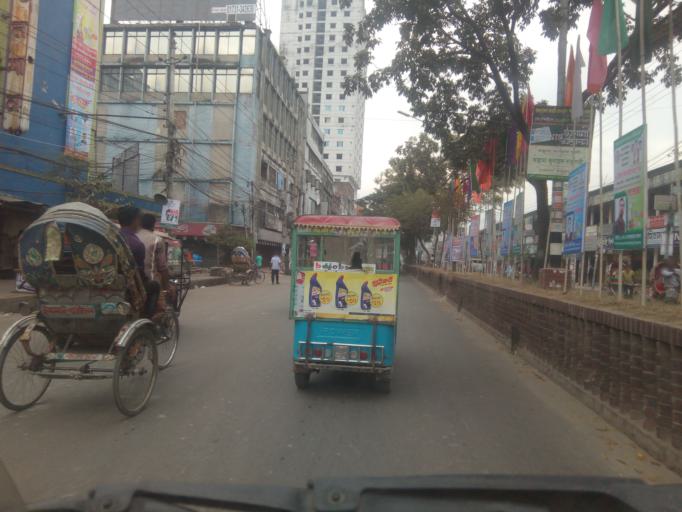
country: BD
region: Dhaka
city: Narayanganj
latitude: 23.6145
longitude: 90.5020
